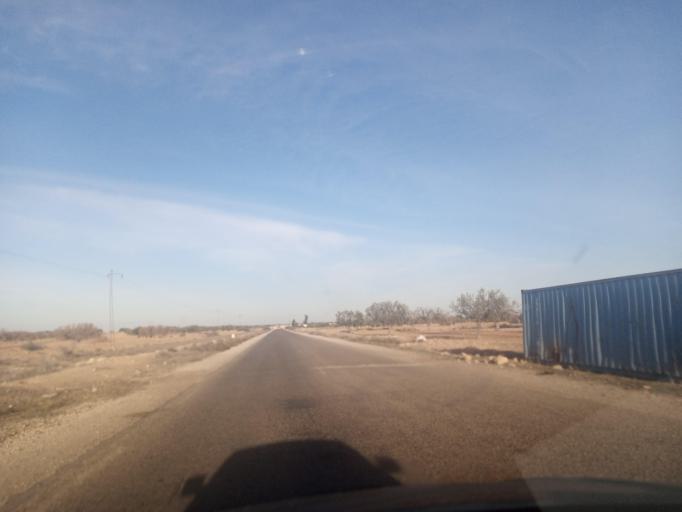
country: TN
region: Safaqis
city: Bi'r `Ali Bin Khalifah
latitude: 34.9448
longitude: 10.3494
